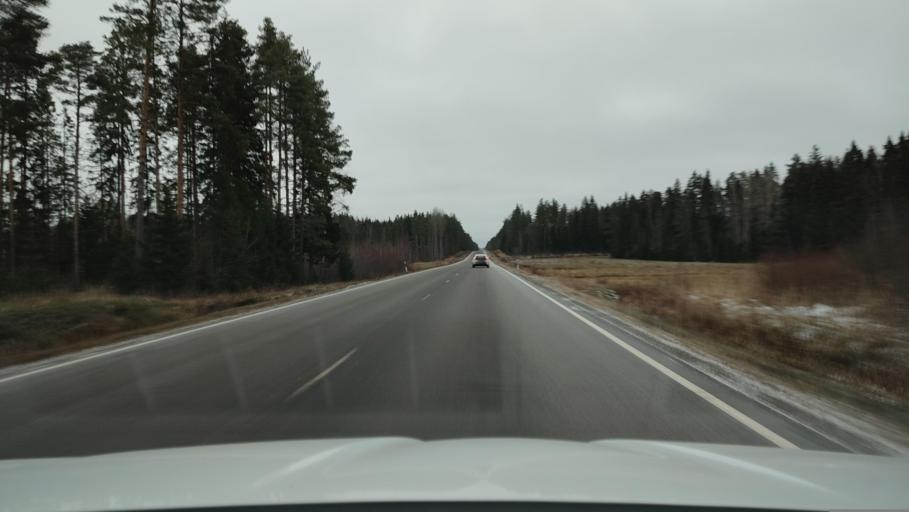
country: FI
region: Ostrobothnia
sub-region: Sydosterbotten
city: Naerpes
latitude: 62.5828
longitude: 21.4953
